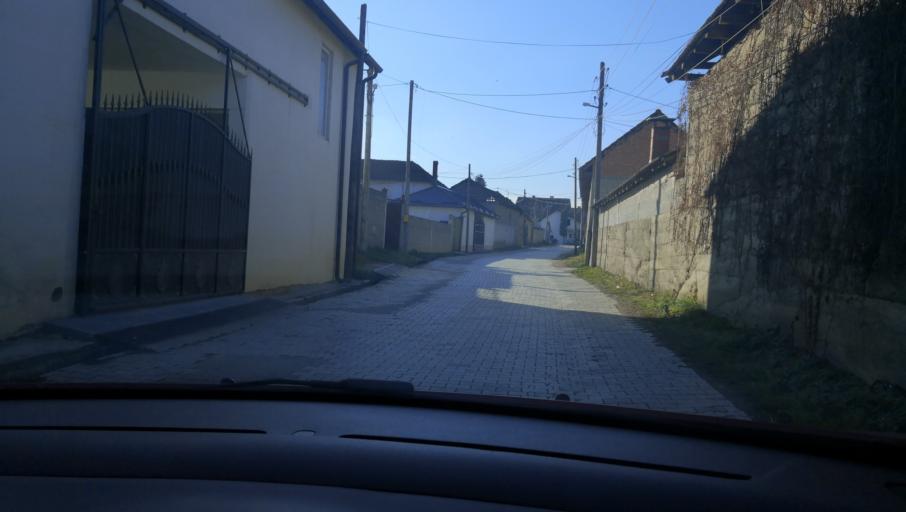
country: MK
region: Brvenica
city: Celopek
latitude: 41.9372
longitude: 21.0070
